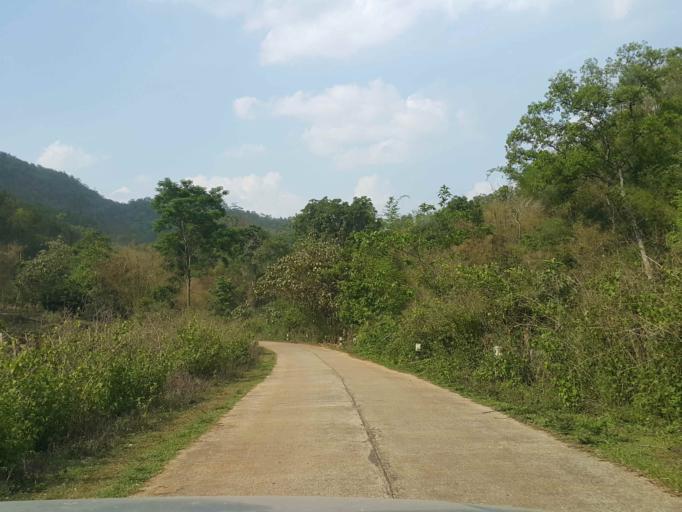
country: TH
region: Chiang Mai
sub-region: Amphoe Chiang Dao
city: Chiang Dao
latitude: 19.4059
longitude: 98.7860
